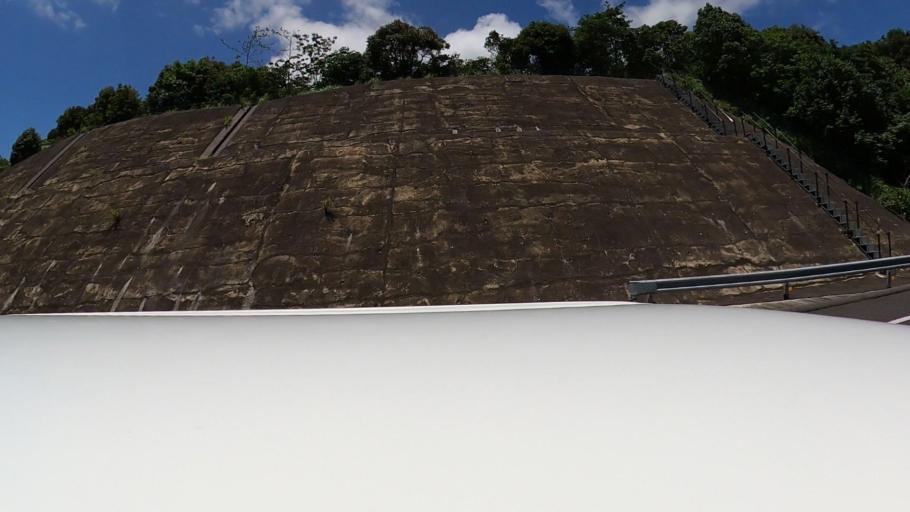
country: JP
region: Miyazaki
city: Nobeoka
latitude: 32.4934
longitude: 131.6551
